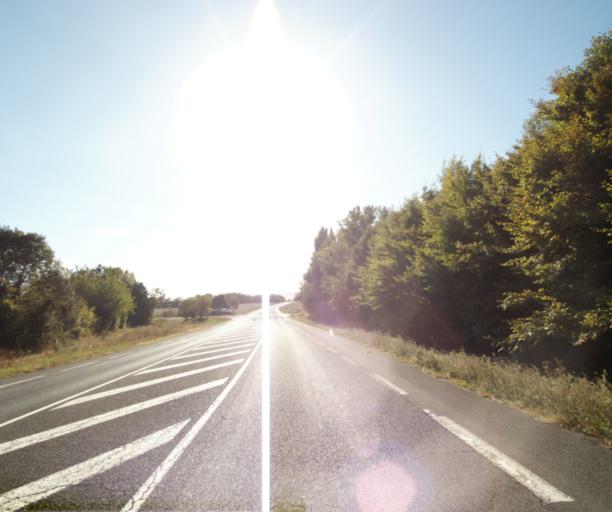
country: FR
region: Auvergne
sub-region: Departement du Puy-de-Dome
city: Malintrat
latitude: 45.8146
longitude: 3.1763
